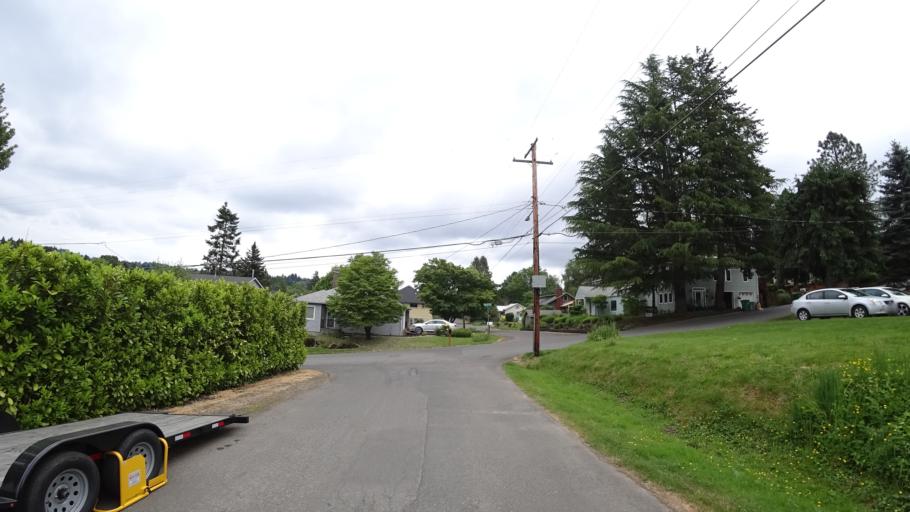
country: US
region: Oregon
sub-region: Washington County
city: Garden Home-Whitford
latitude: 45.4754
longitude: -122.7339
